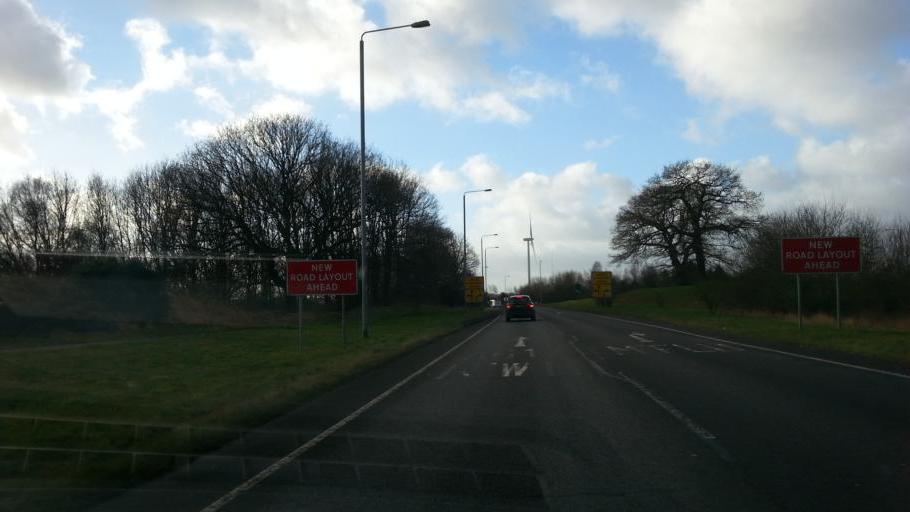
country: GB
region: England
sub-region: Nottinghamshire
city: Rainworth
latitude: 53.1270
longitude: -1.1402
